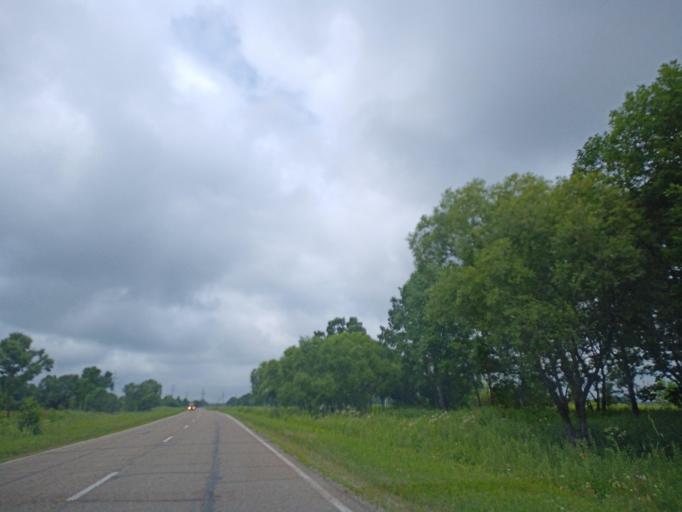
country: RU
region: Primorskiy
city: Dal'nerechensk
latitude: 45.9502
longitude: 133.9209
